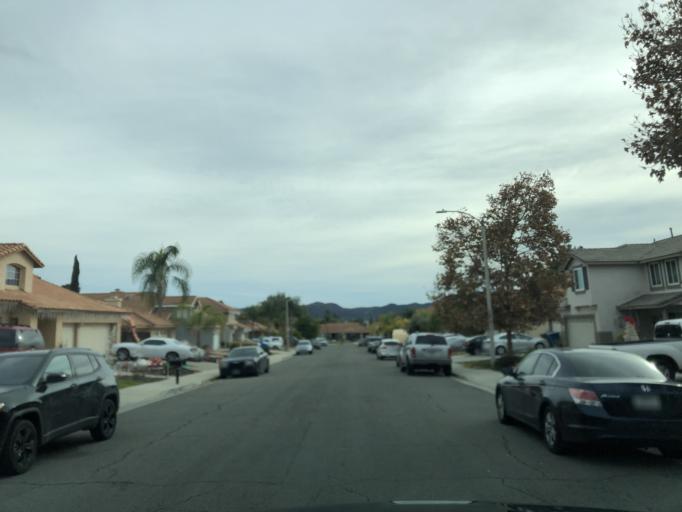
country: US
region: California
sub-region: Riverside County
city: Wildomar
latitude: 33.6083
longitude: -117.2631
